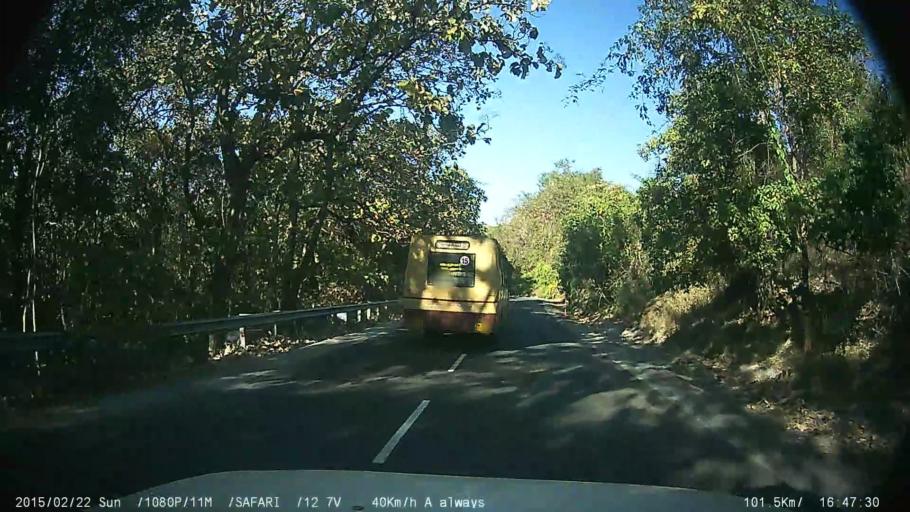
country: IN
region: Tamil Nadu
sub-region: Theni
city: Gudalur
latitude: 9.6227
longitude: 77.1937
